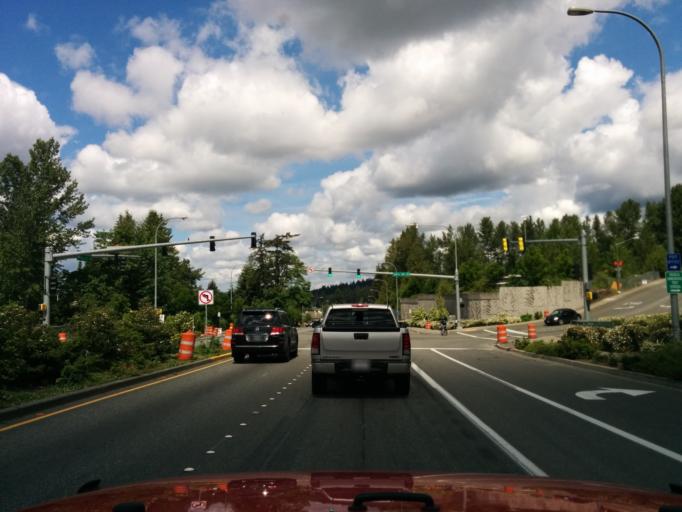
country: US
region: Washington
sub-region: King County
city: Sammamish
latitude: 47.6604
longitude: -122.0942
